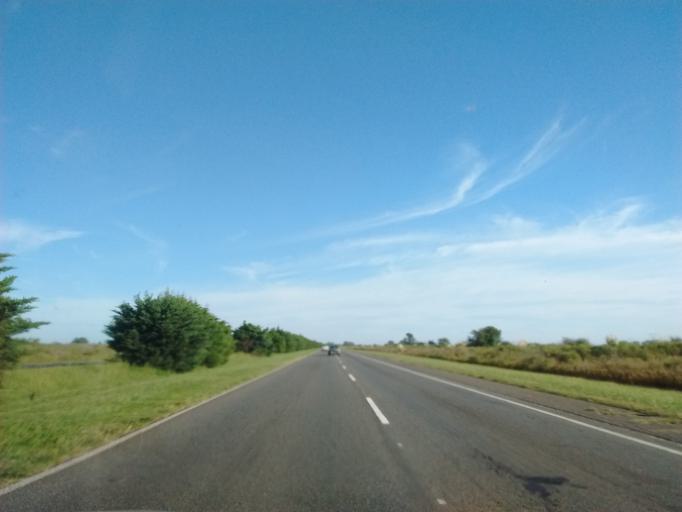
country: AR
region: Santa Fe
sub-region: Departamento de San Lorenzo
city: San Lorenzo
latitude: -32.5935
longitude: -60.8624
